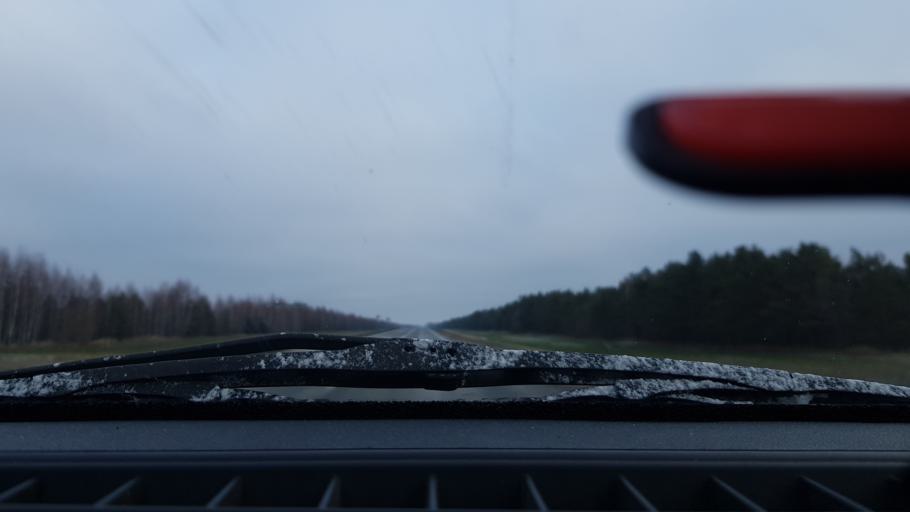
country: RU
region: Tatarstan
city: Kuybyshevskiy Zaton
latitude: 54.9548
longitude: 49.4747
